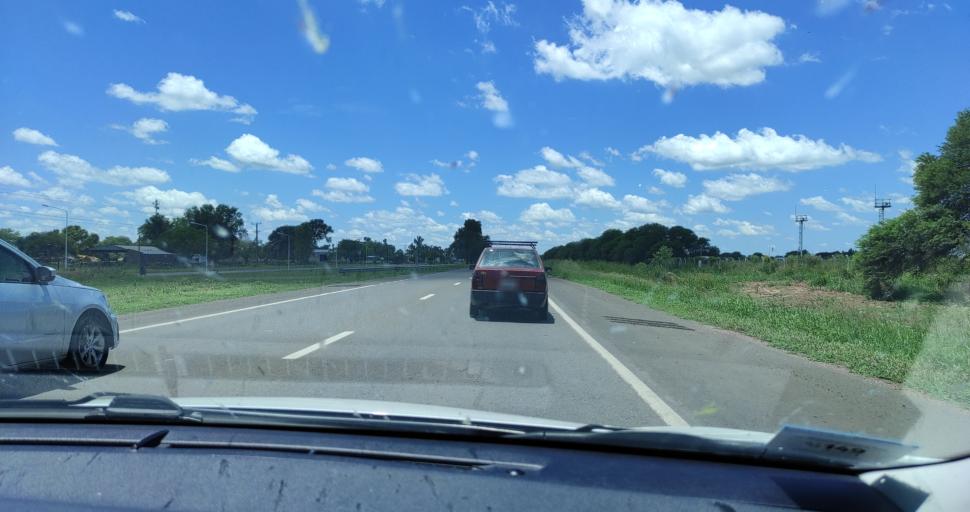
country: AR
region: Chaco
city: Avia Terai
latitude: -26.7030
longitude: -60.7355
